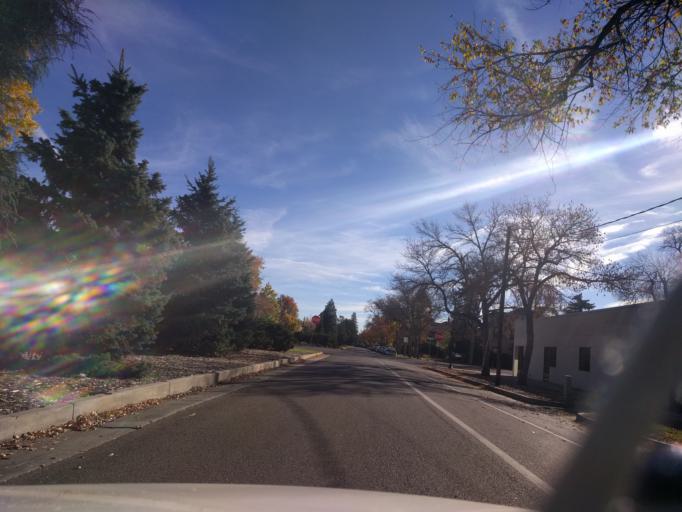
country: US
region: Colorado
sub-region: El Paso County
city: Colorado Springs
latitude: 38.8423
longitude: -104.8239
